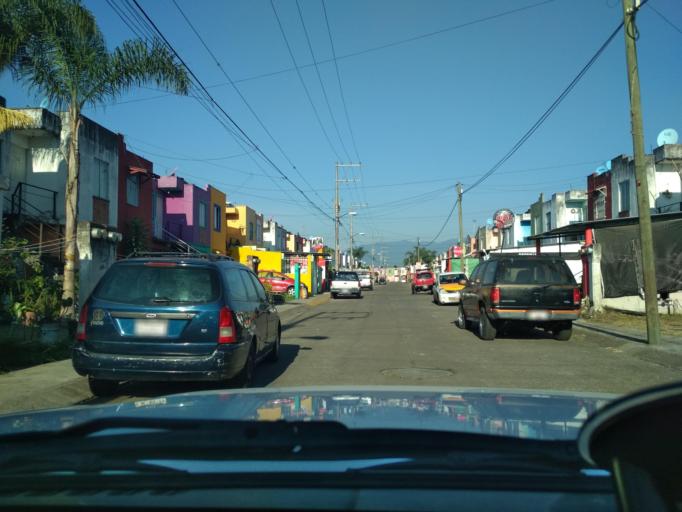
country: MX
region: Veracruz
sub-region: Fortin
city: Fraccionamiento Villas de la Llave
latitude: 18.9193
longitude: -96.9916
